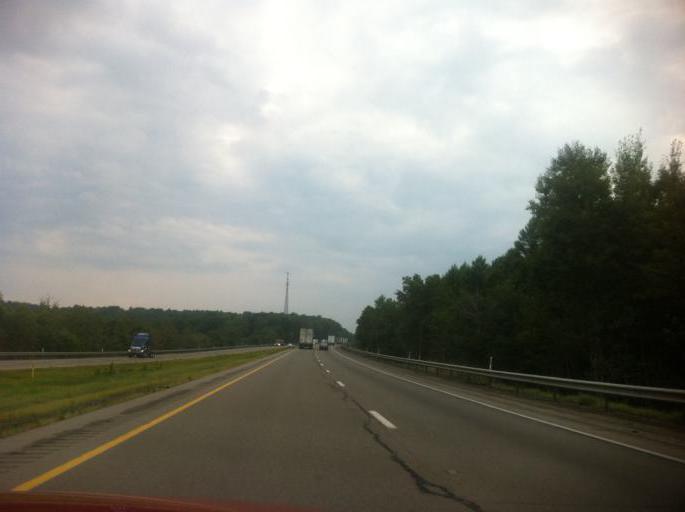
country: US
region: Pennsylvania
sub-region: Jefferson County
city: Brookville
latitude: 41.1826
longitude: -79.1524
